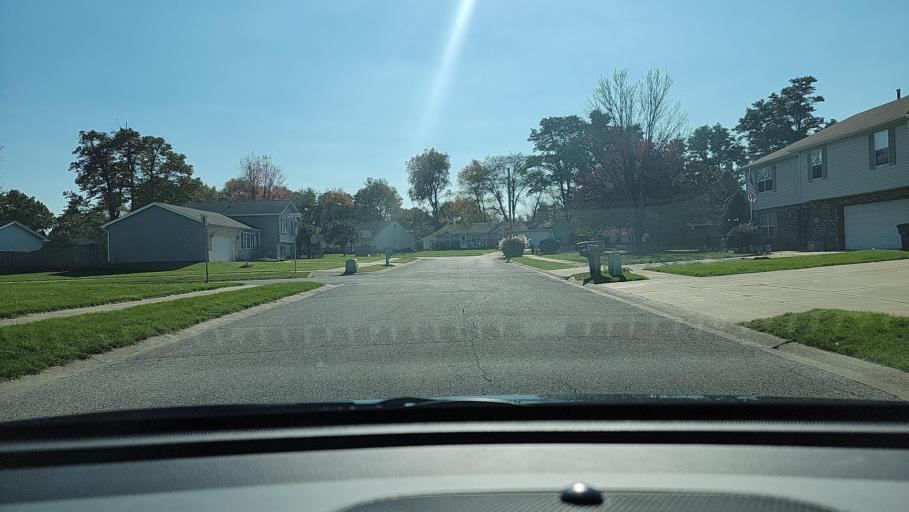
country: US
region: Indiana
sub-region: Porter County
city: Portage
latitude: 41.5803
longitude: -87.1608
